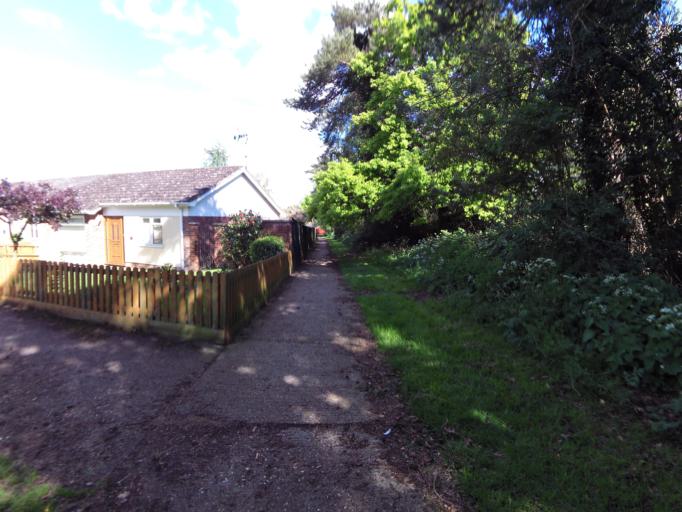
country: GB
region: England
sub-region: Suffolk
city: Thurston
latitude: 52.2494
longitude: 0.8218
